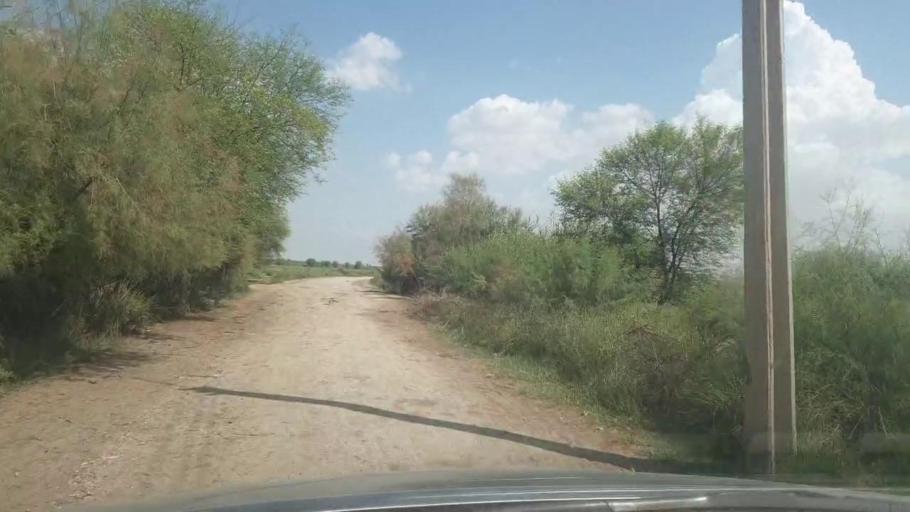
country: PK
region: Sindh
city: Khairpur
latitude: 27.5465
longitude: 68.8031
